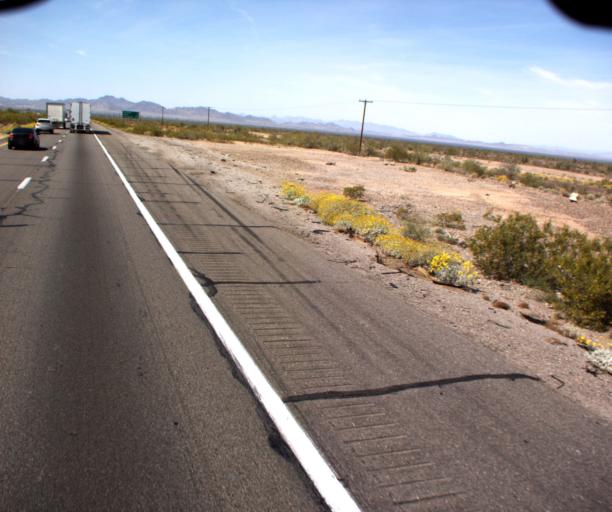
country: US
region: Arizona
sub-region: La Paz County
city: Quartzsite
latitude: 33.6793
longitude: -114.0965
